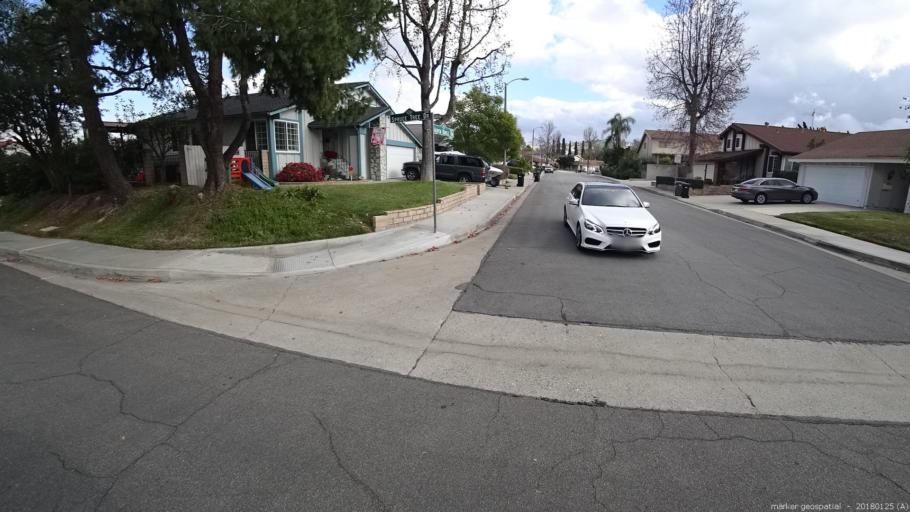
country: US
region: California
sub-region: Los Angeles County
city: Diamond Bar
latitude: 33.9979
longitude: -117.8168
